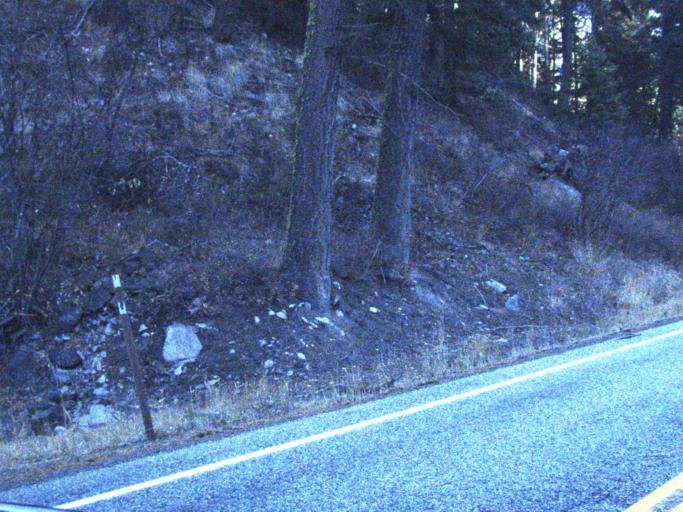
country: US
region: Washington
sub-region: Ferry County
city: Republic
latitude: 48.5994
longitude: -118.6230
